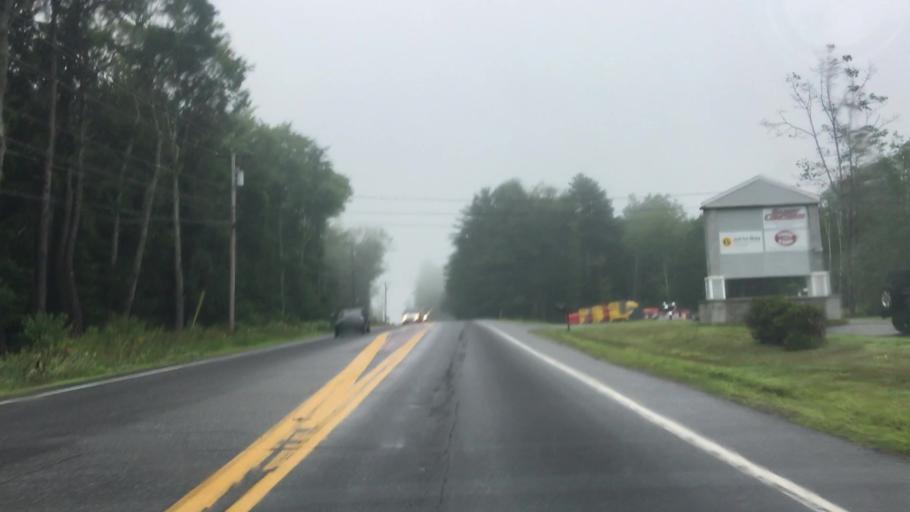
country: US
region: Maine
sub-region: Lincoln County
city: Wiscasset
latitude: 43.9820
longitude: -69.7009
